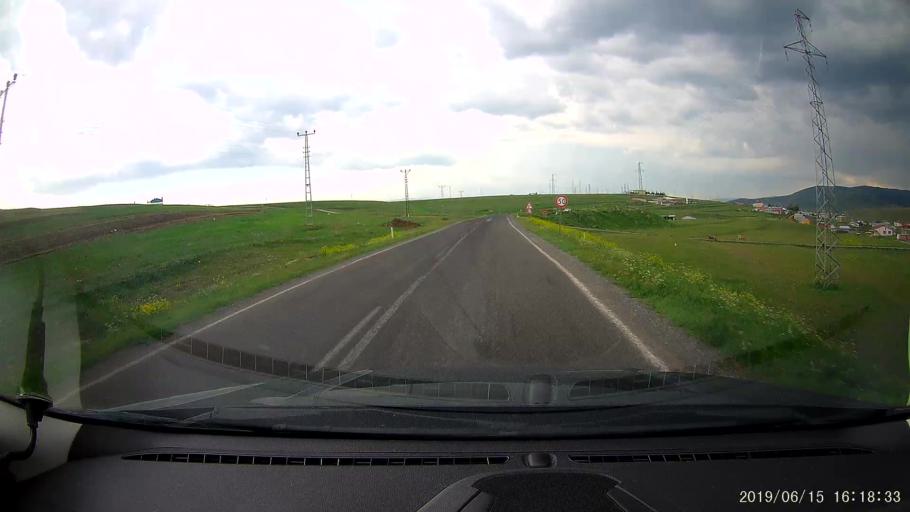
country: TR
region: Ardahan
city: Hanak
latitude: 41.2383
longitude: 42.8518
